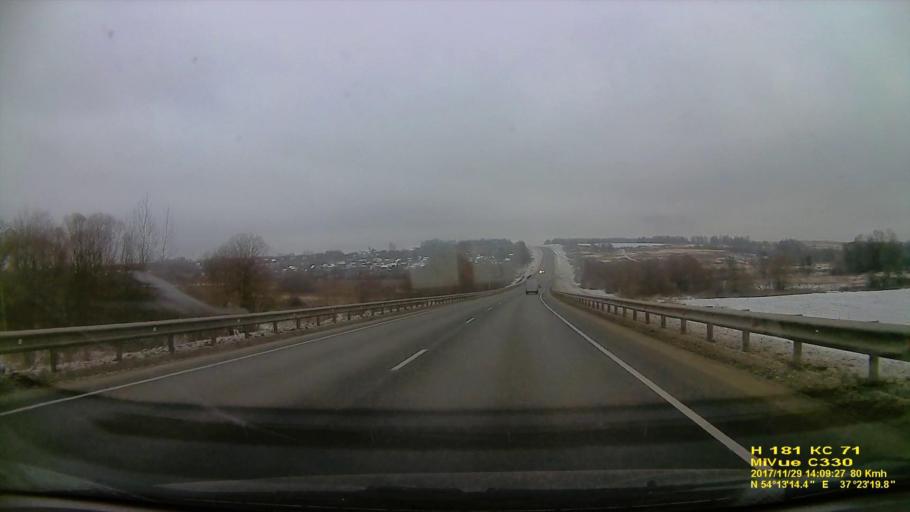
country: RU
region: Tula
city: Leninskiy
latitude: 54.2204
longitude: 37.3891
